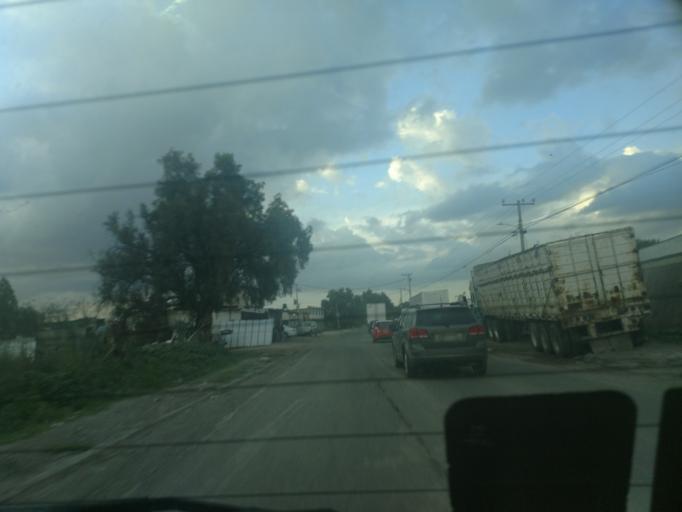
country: MX
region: Mexico
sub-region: Cuautitlan
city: Barrio Tlatenco
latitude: 19.7563
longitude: -99.2013
